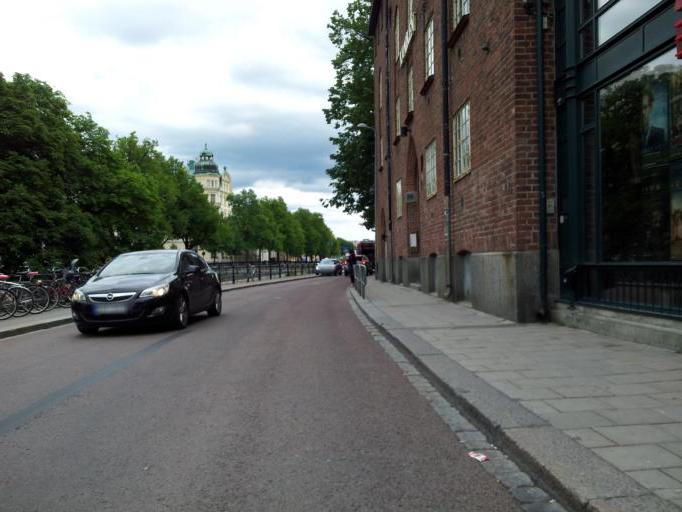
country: SE
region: Uppsala
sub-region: Uppsala Kommun
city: Uppsala
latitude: 59.8572
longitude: 17.6383
